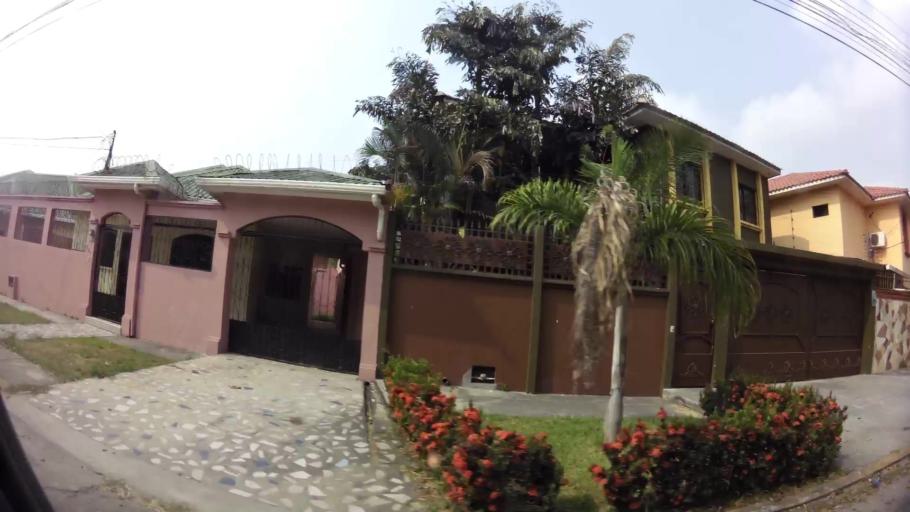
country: HN
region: Cortes
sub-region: San Pedro Sula
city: Pena Blanca
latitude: 15.5371
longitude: -88.0254
